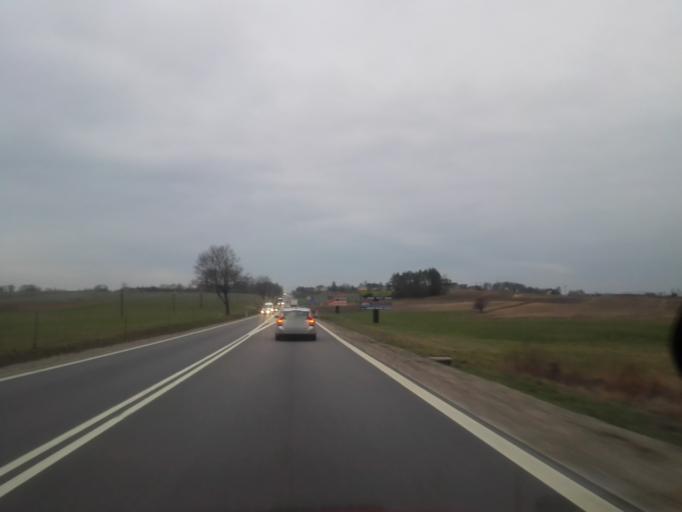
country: PL
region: Podlasie
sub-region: Powiat lomzynski
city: Piatnica
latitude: 53.2373
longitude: 22.1149
